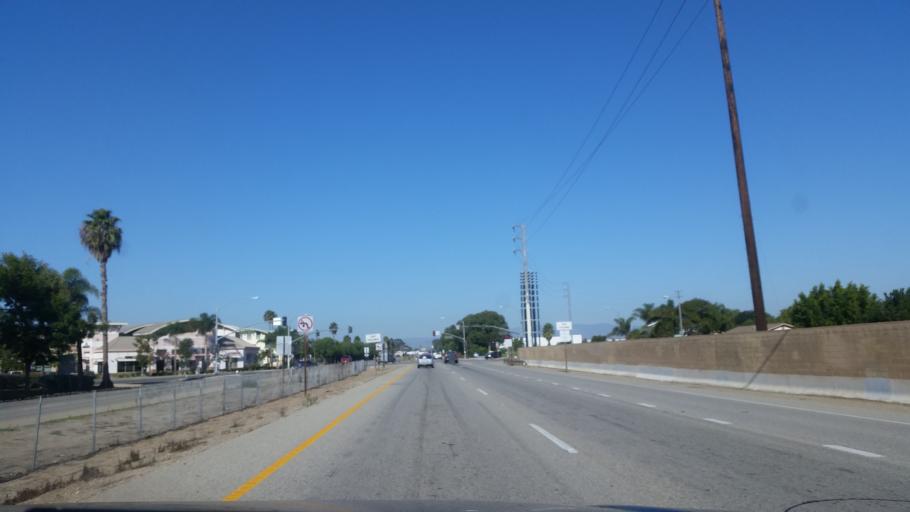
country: US
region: California
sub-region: Ventura County
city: Oxnard
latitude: 34.1745
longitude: -119.1588
